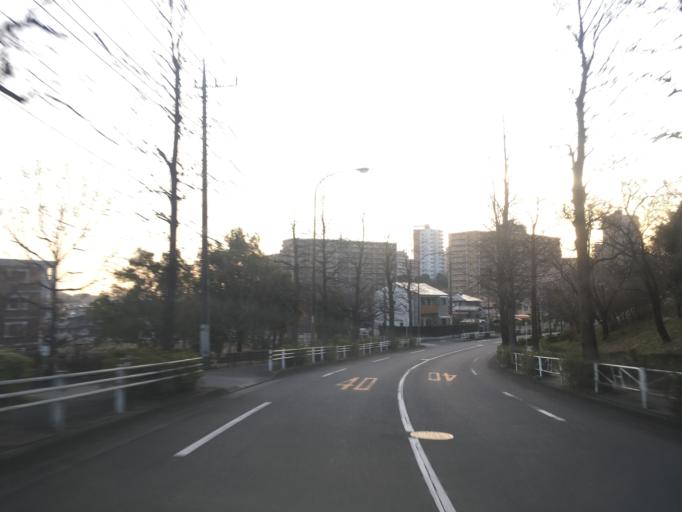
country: JP
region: Tokyo
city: Hino
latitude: 35.6208
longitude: 139.3740
